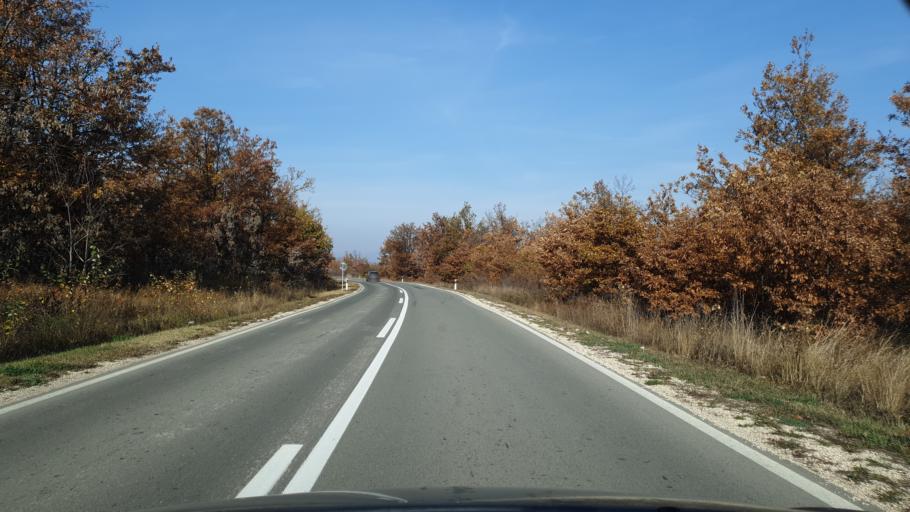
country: RS
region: Central Serbia
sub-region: Borski Okrug
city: Bor
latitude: 44.0092
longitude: 22.0721
